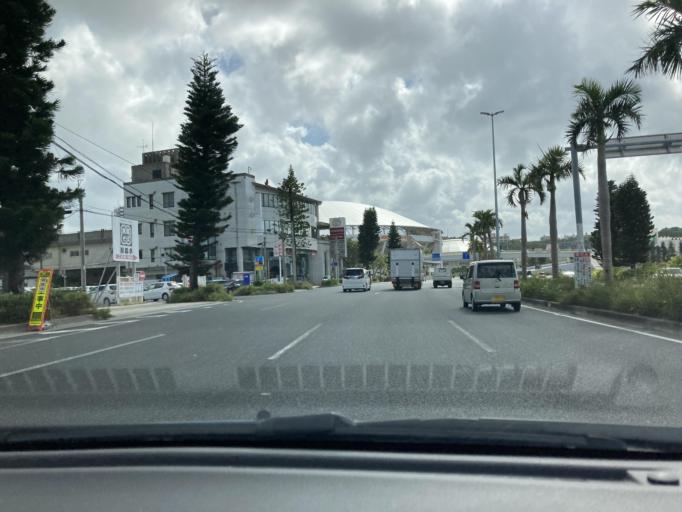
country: JP
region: Okinawa
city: Naha-shi
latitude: 26.2063
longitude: 127.6739
